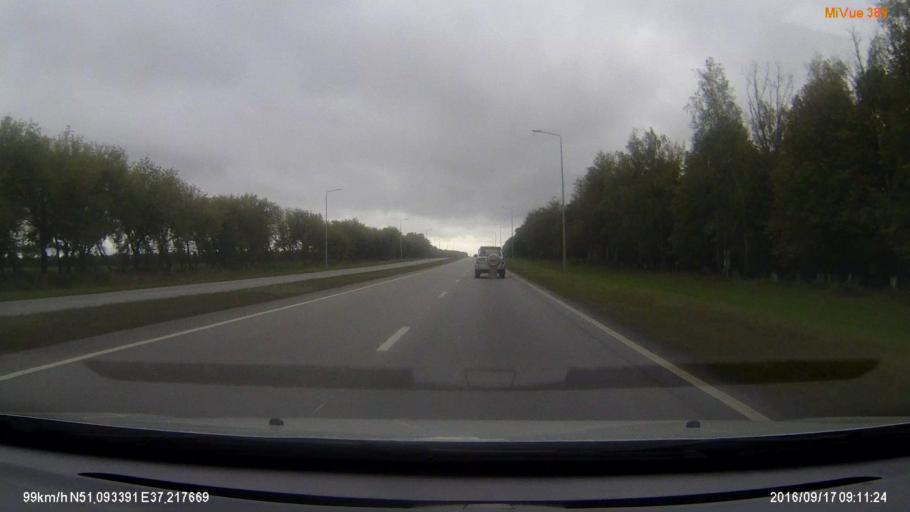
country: RU
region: Belgorod
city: Skorodnoye
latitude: 51.0931
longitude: 37.2175
